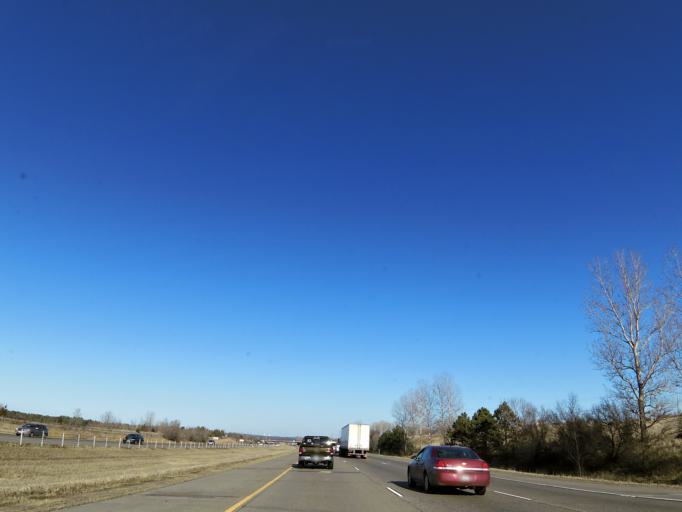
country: US
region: Minnesota
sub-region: Washington County
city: Lakeland
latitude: 44.9510
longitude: -92.8091
